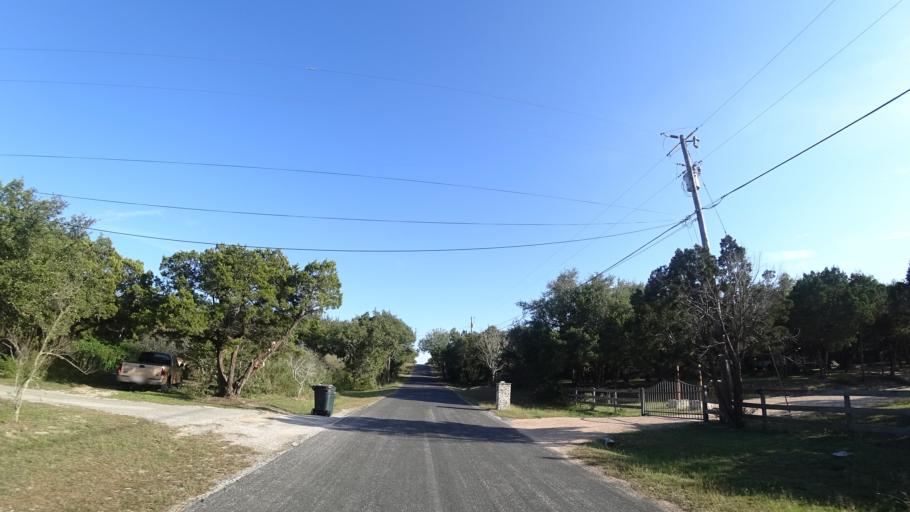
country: US
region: Texas
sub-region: Travis County
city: Barton Creek
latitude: 30.2402
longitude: -97.9161
